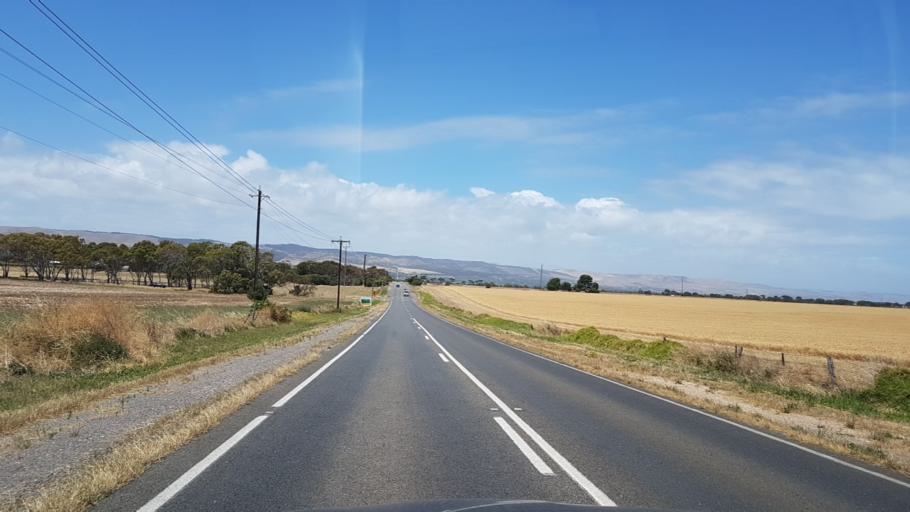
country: AU
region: South Australia
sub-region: Onkaparinga
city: Aldinga
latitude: -35.2522
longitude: 138.4821
